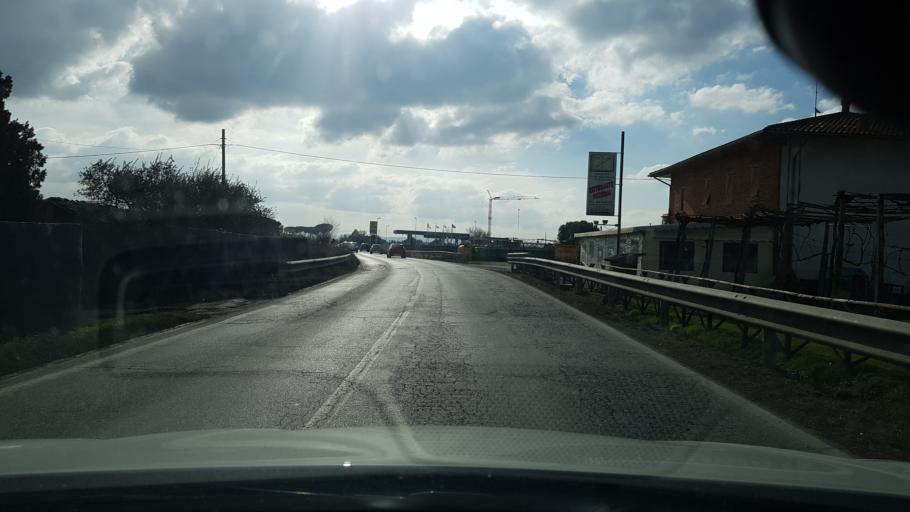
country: IT
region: Umbria
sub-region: Provincia di Perugia
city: Castiglione del Lago
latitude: 43.1512
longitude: 12.0208
